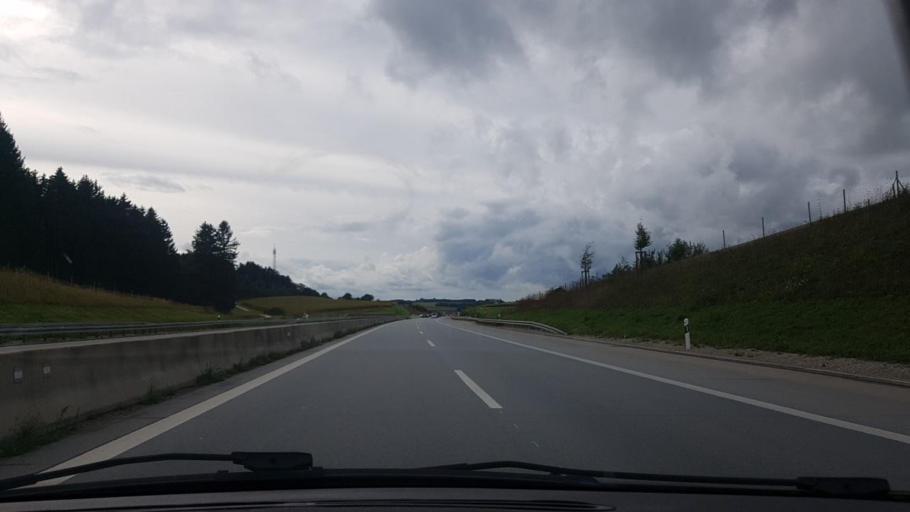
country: DE
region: Bavaria
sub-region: Upper Bavaria
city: Lengdorf
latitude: 48.2482
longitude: 12.0649
